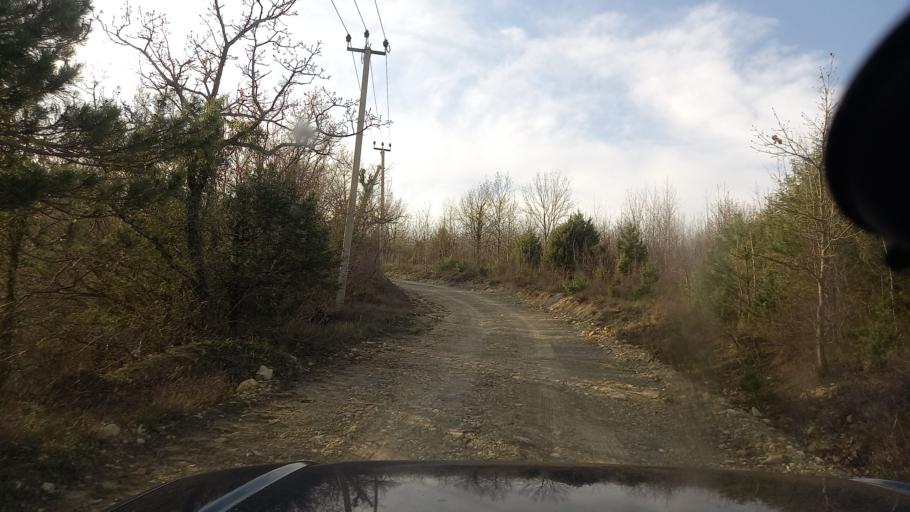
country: RU
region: Krasnodarskiy
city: Arkhipo-Osipovka
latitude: 44.3626
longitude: 38.5726
